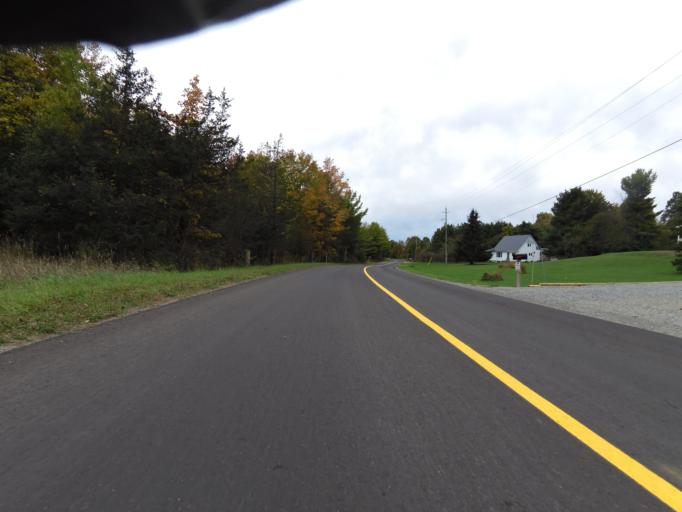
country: CA
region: Ontario
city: Gananoque
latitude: 44.5815
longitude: -76.0632
